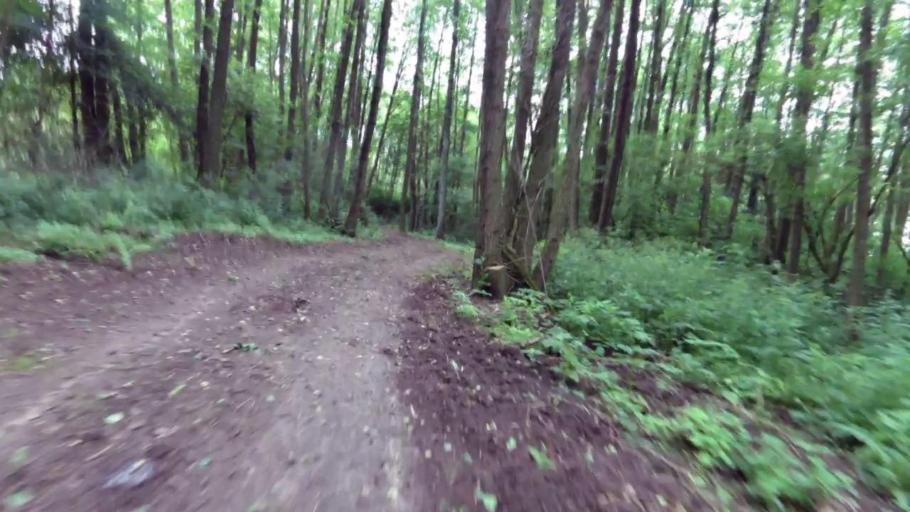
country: PL
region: West Pomeranian Voivodeship
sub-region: Powiat stargardzki
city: Chociwel
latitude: 53.4621
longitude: 15.3511
